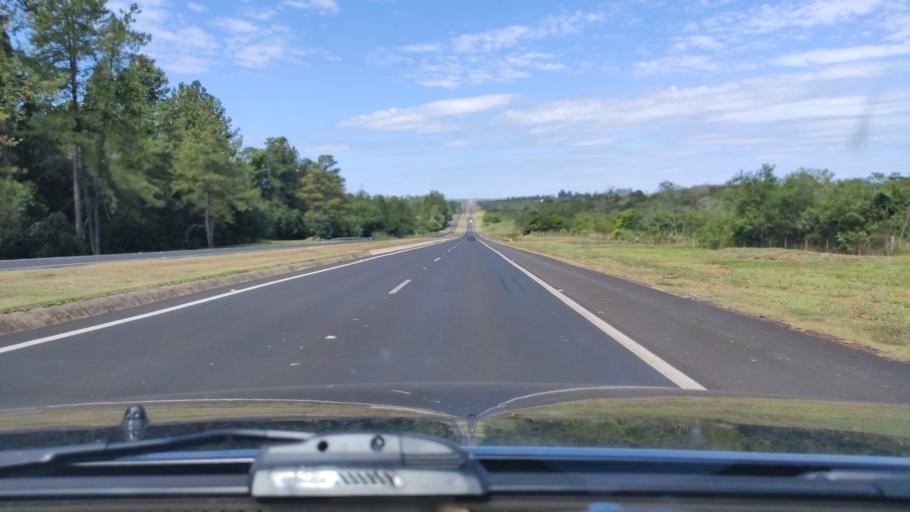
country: BR
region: Sao Paulo
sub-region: Rancharia
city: Rancharia
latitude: -22.4680
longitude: -50.9515
